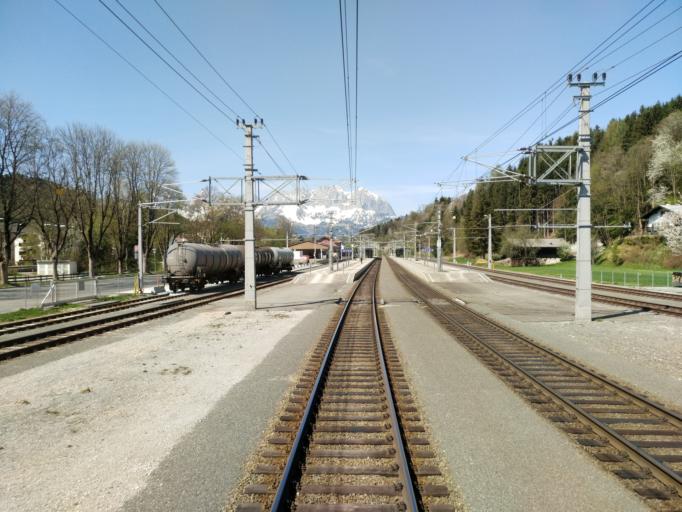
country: AT
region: Tyrol
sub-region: Politischer Bezirk Kitzbuhel
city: Kitzbuhel
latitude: 47.4519
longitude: 12.3916
